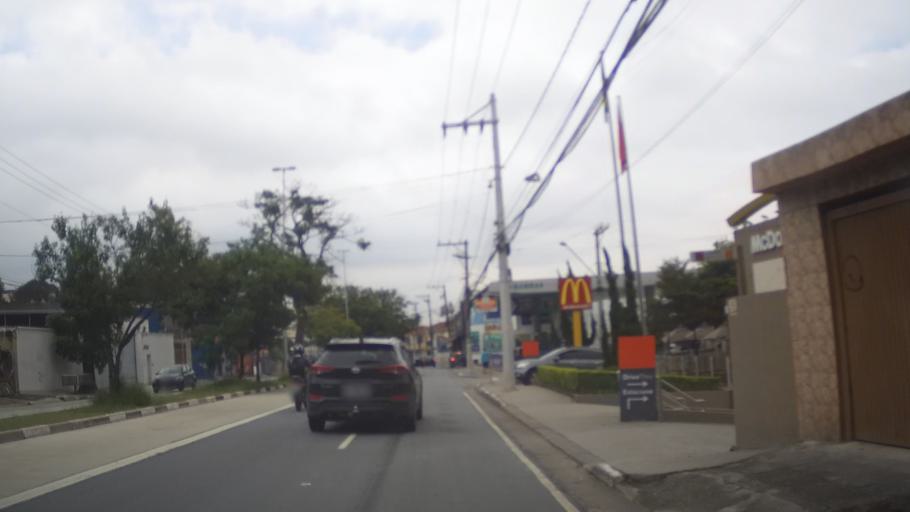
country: BR
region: Sao Paulo
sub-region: Guarulhos
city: Guarulhos
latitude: -23.4746
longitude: -46.5469
